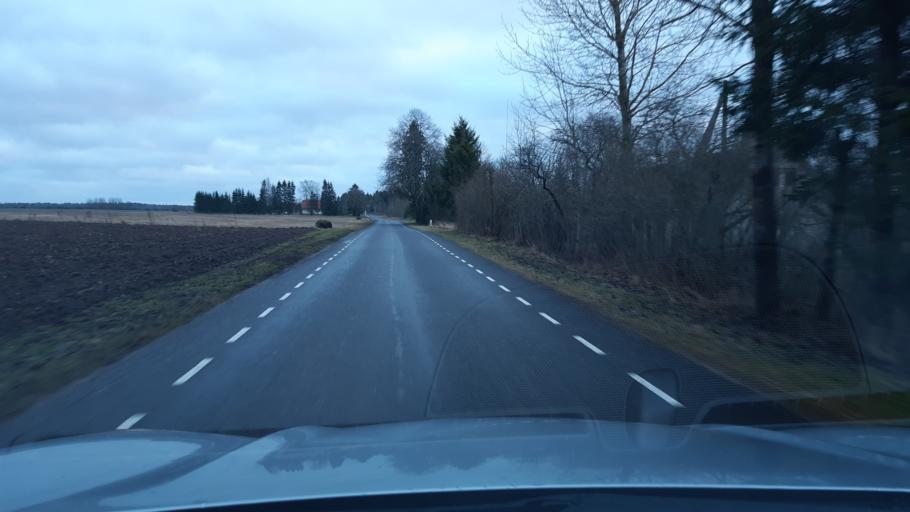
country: EE
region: Harju
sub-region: Saue linn
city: Saue
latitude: 59.2372
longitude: 24.4993
